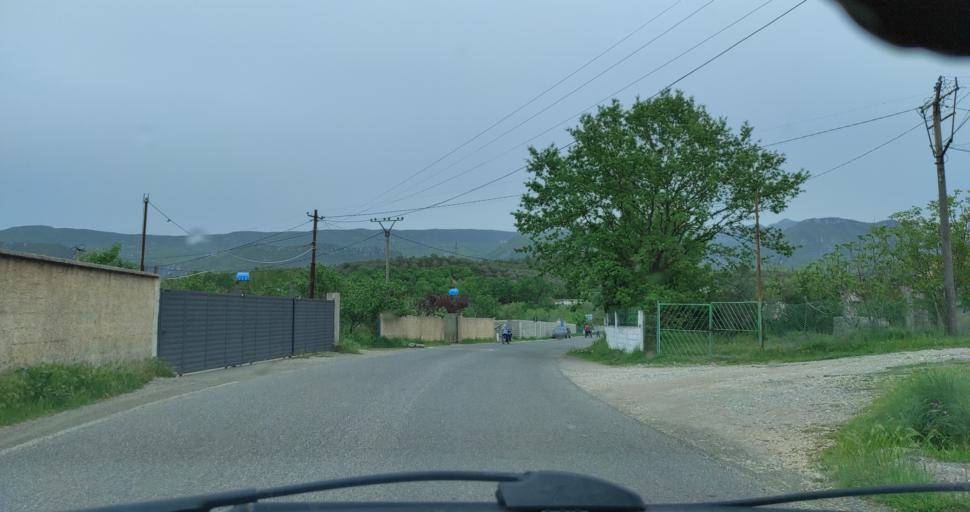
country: AL
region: Lezhe
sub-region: Rrethi i Kurbinit
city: Mamurras
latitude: 41.5891
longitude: 19.6957
